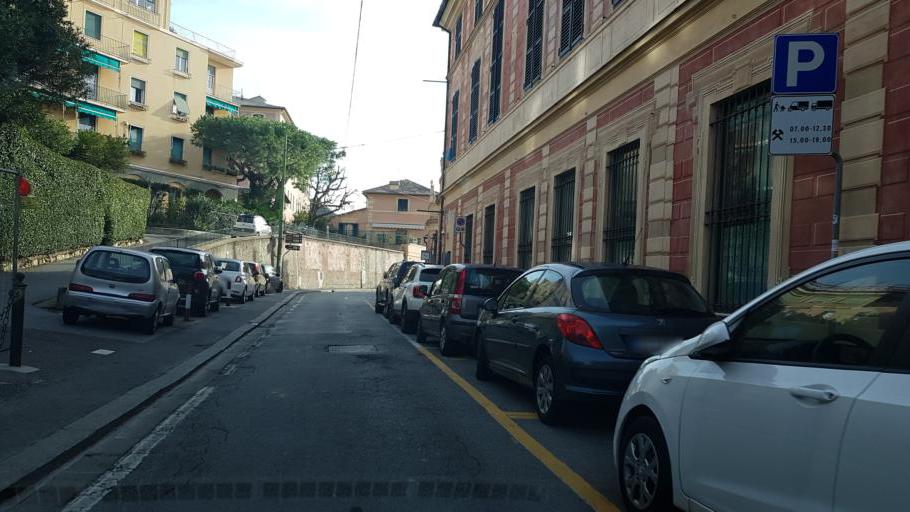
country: IT
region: Liguria
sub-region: Provincia di Genova
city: Bogliasco
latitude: 44.3824
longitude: 9.0454
